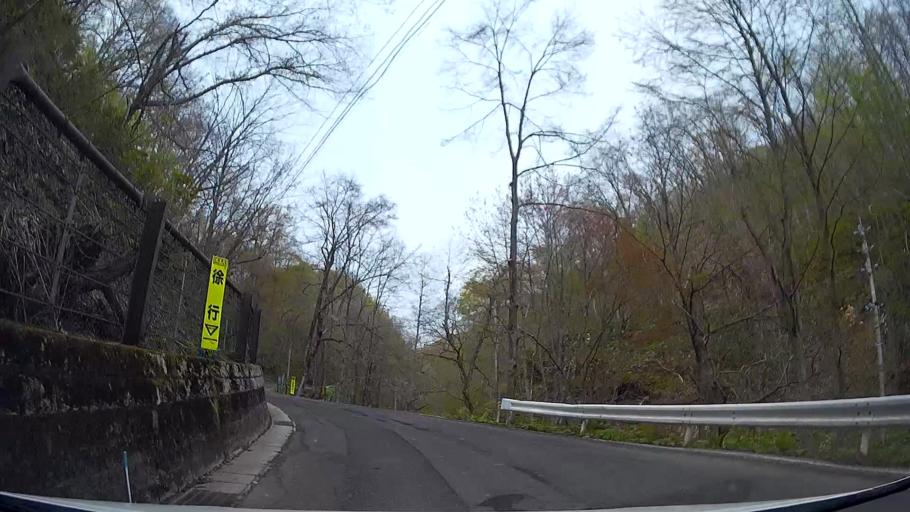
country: JP
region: Akita
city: Hanawa
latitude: 40.3840
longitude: 140.8859
